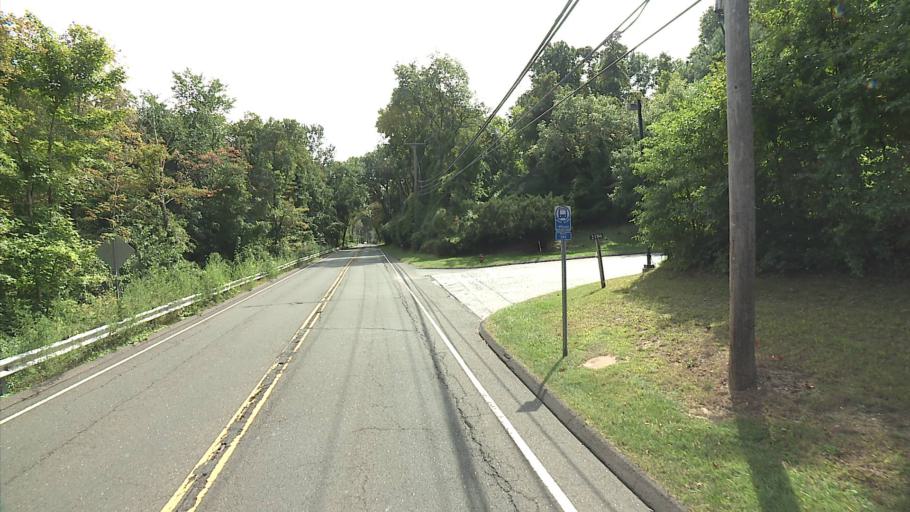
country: US
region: Connecticut
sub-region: Fairfield County
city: North Stamford
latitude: 41.1448
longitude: -73.5473
